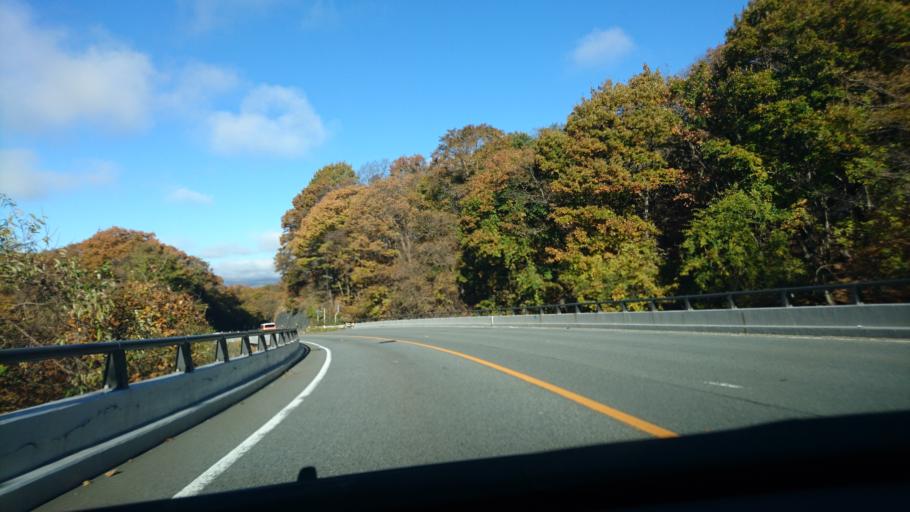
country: JP
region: Nagano
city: Saku
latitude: 36.3256
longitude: 138.6481
